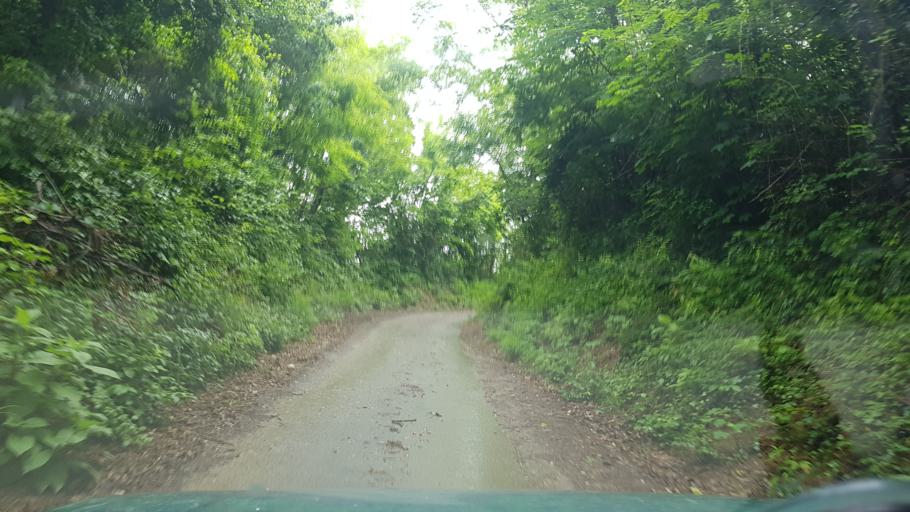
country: IT
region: Friuli Venezia Giulia
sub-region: Provincia di Gorizia
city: Gorizia
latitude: 45.9465
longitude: 13.5921
